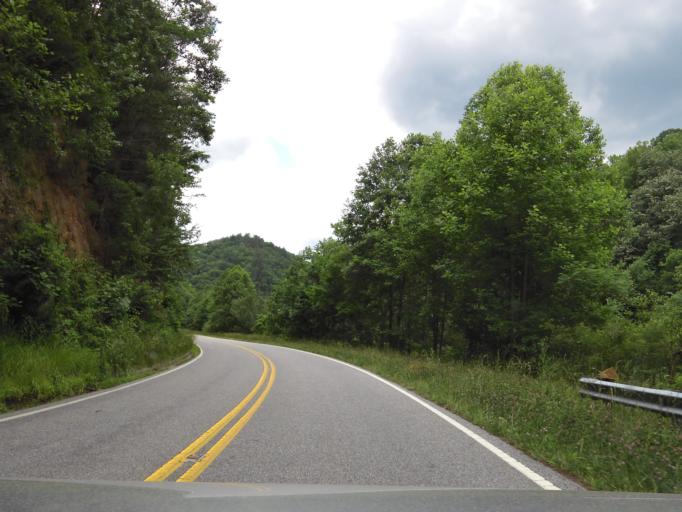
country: US
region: North Carolina
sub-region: Graham County
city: Robbinsville
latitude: 35.4218
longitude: -83.8944
